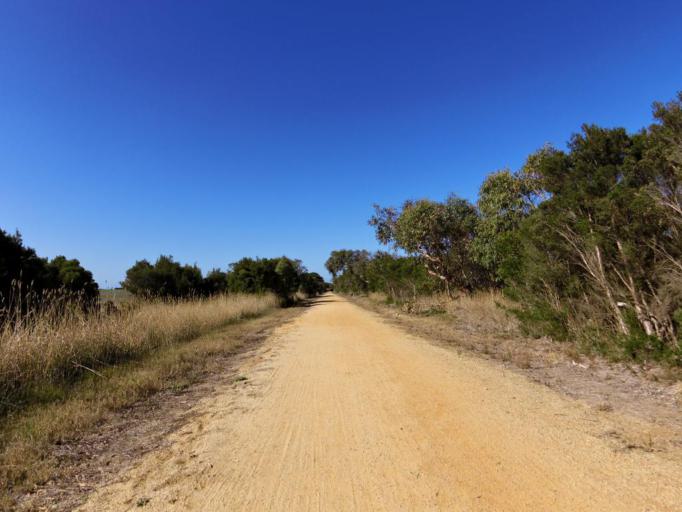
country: AU
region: Victoria
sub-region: Bass Coast
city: North Wonthaggi
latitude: -38.5847
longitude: 145.5553
